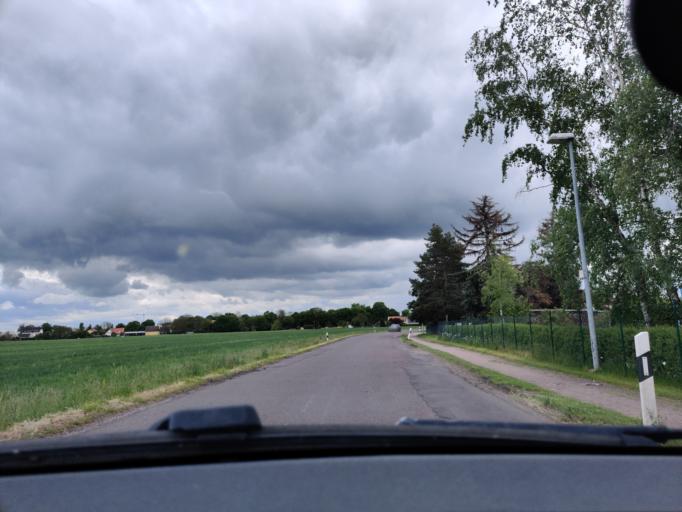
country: DE
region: Saxony-Anhalt
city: Schonebeck
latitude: 51.9795
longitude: 11.7718
